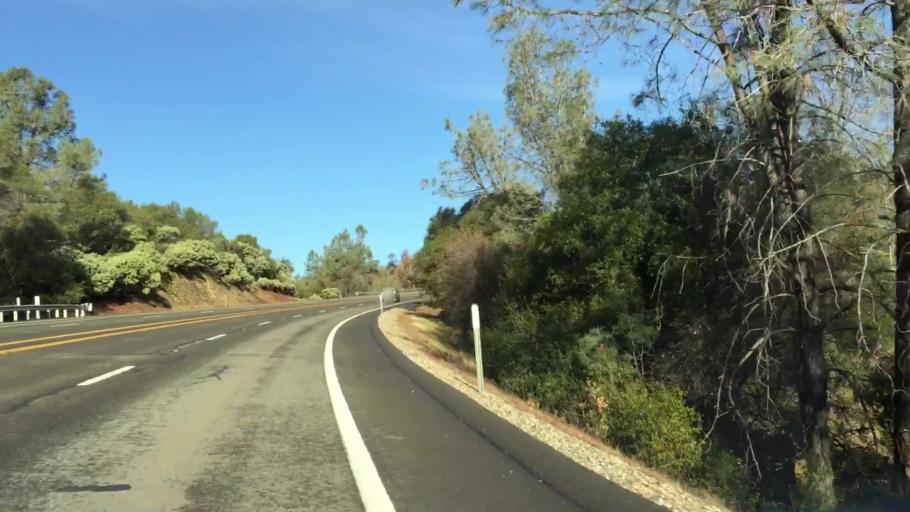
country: US
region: California
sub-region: Butte County
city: Paradise
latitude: 39.6805
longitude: -121.5459
